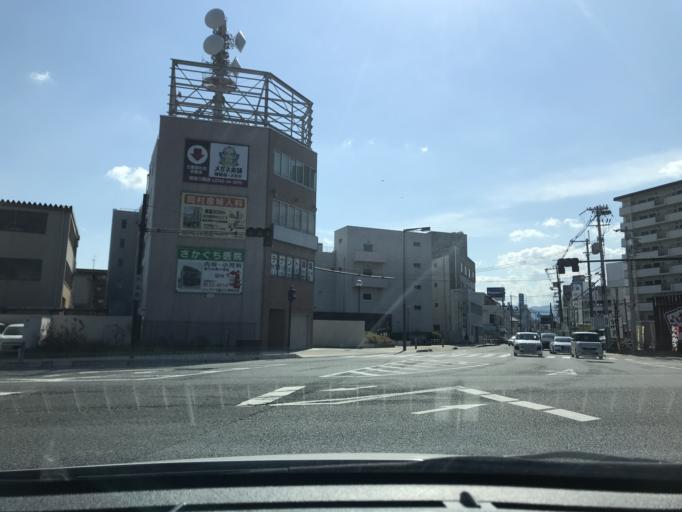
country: JP
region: Nara
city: Nara-shi
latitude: 34.6768
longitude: 135.8195
